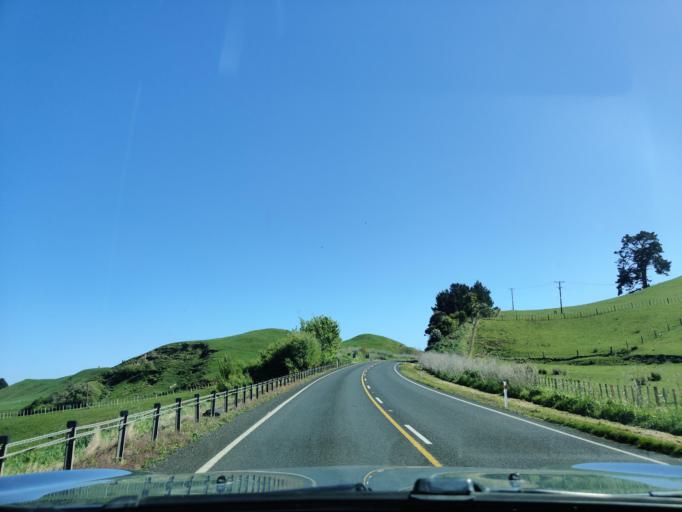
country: NZ
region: Manawatu-Wanganui
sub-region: Wanganui District
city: Wanganui
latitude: -39.9669
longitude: 175.1019
